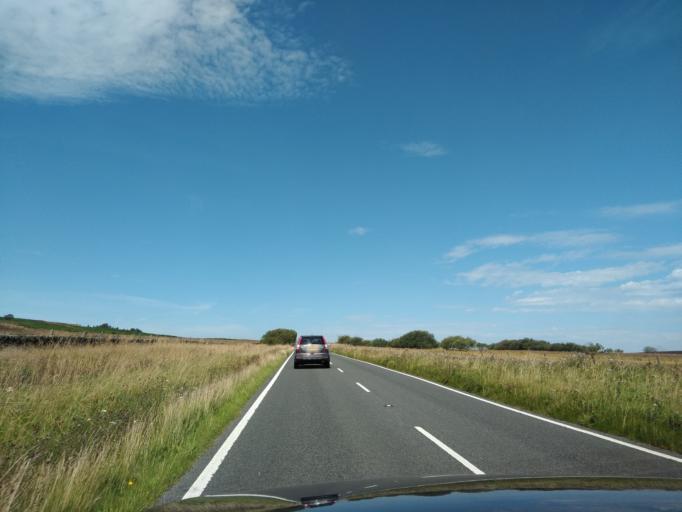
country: GB
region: England
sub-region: Derbyshire
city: Hathersage
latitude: 53.3015
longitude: -1.5891
